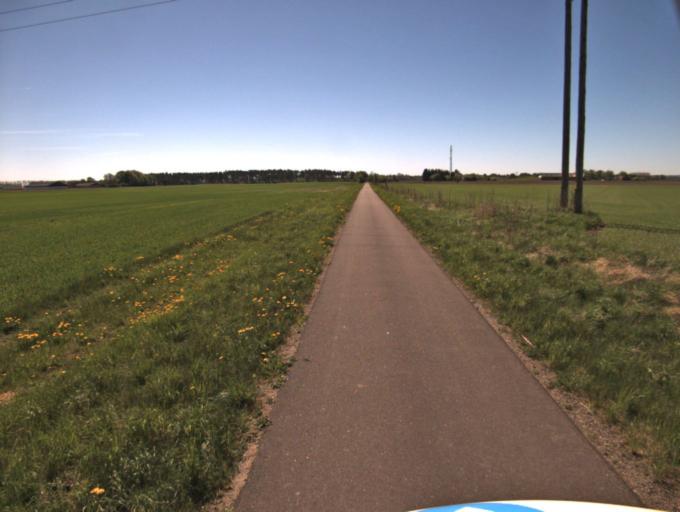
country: SE
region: Skane
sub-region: Kristianstads Kommun
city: Norra Asum
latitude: 55.9605
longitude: 14.1577
